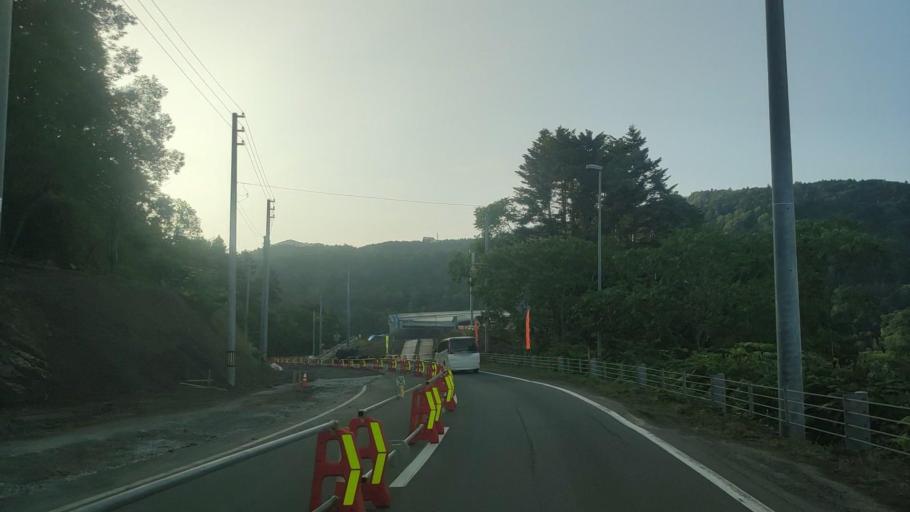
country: JP
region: Hokkaido
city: Bibai
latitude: 43.2327
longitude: 142.0389
